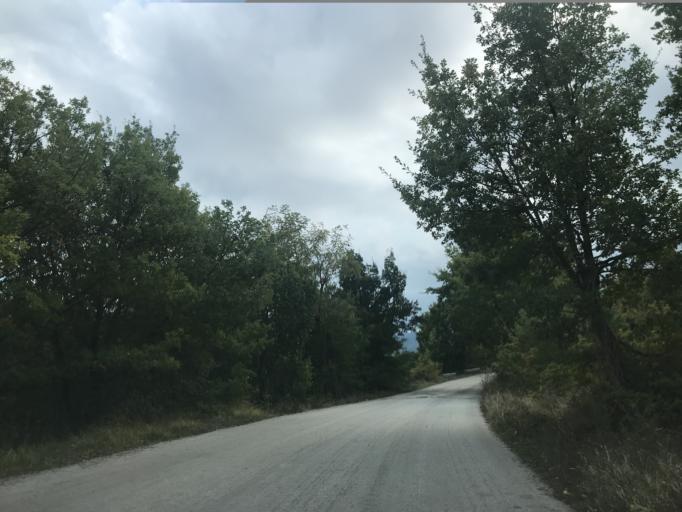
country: IT
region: Molise
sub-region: Provincia di Isernia
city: Bagnoli del Trigno
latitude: 41.6831
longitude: 14.4560
